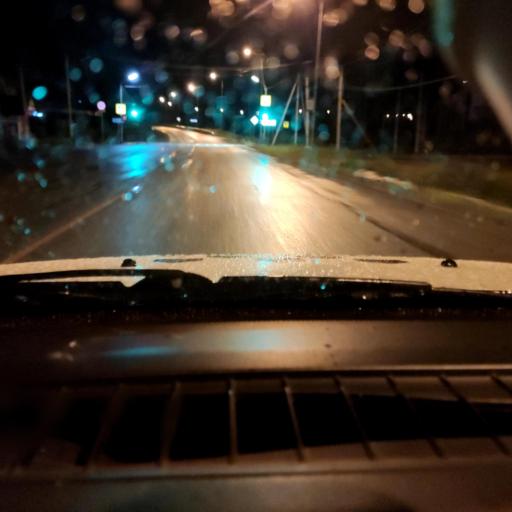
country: RU
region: Udmurtiya
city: Khokhryaki
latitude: 57.1826
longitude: 53.1562
